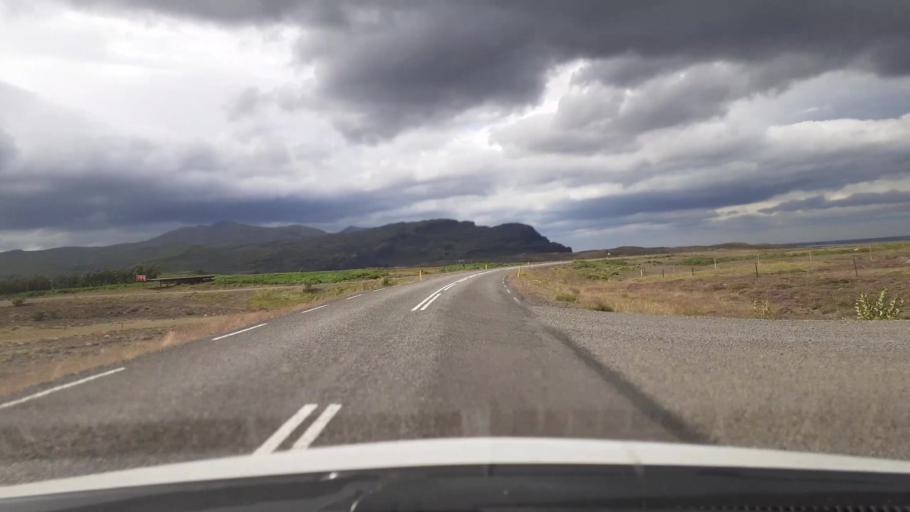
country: IS
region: West
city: Borgarnes
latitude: 64.5450
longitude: -21.6591
